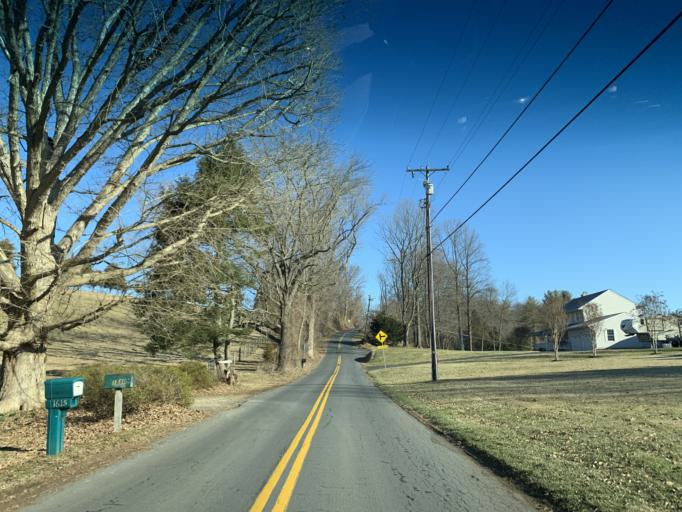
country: US
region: Maryland
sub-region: Harford County
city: Aberdeen
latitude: 39.6033
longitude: -76.2245
